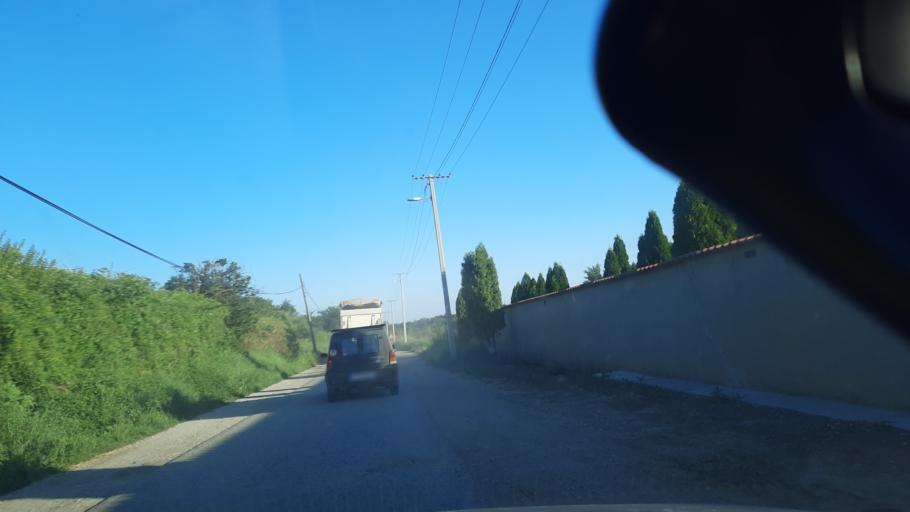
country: RS
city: Cortanovci
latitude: 45.1210
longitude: 19.9439
